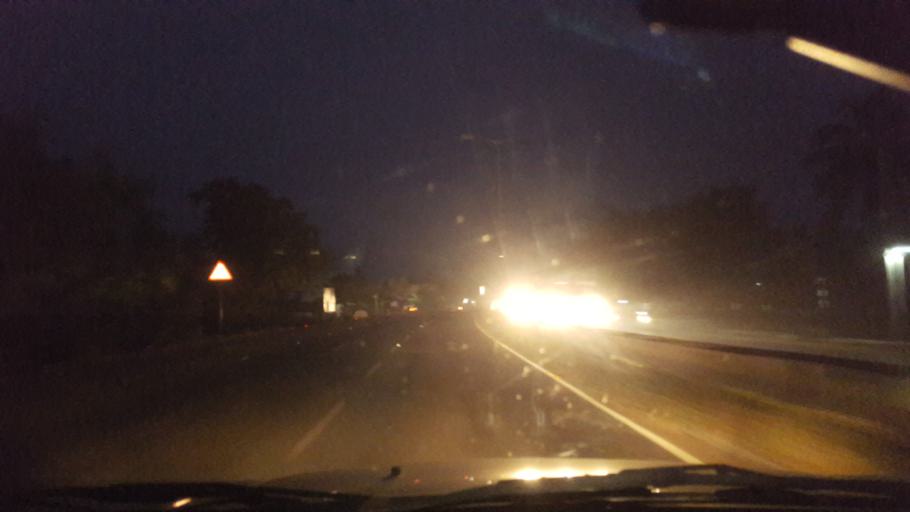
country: IN
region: Andhra Pradesh
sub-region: East Godavari
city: Peddapuram
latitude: 17.1355
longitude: 81.9559
